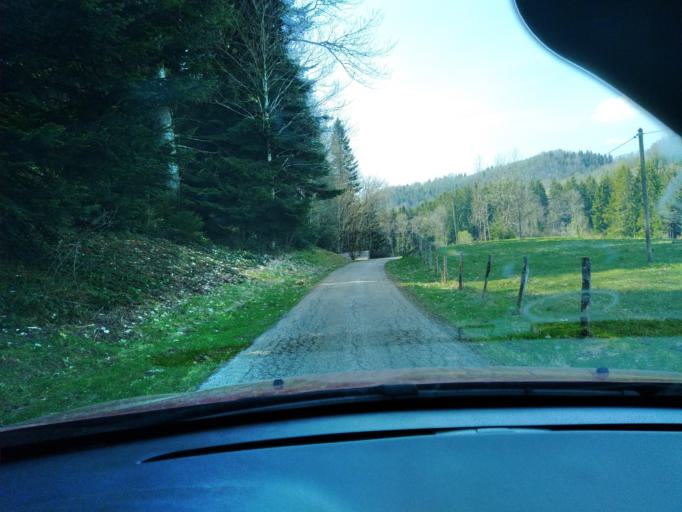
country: FR
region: Franche-Comte
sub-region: Departement du Jura
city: Lavans-les-Saint-Claude
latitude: 46.3978
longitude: 5.7528
